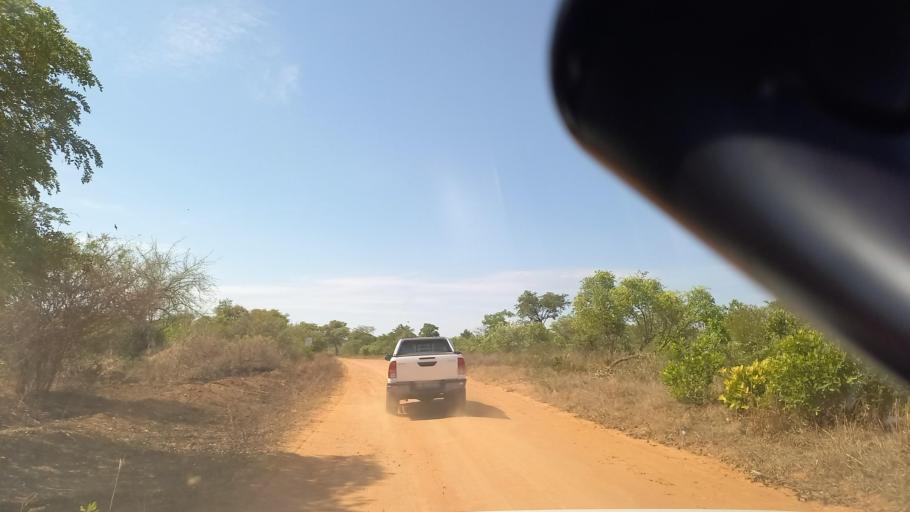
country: ZM
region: Southern
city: Mazabuka
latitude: -16.0352
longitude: 27.6176
